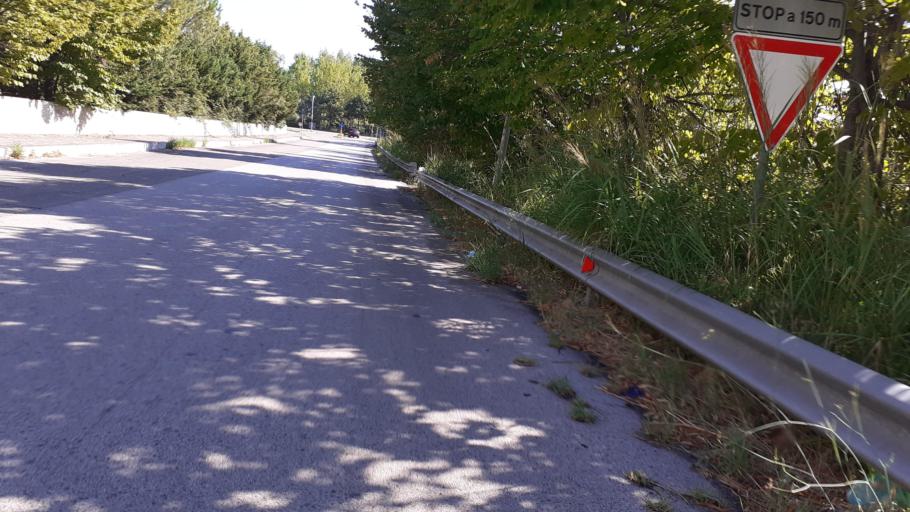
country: IT
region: Abruzzo
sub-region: Provincia di Chieti
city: Marina di Vasto
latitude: 42.0813
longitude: 14.7413
